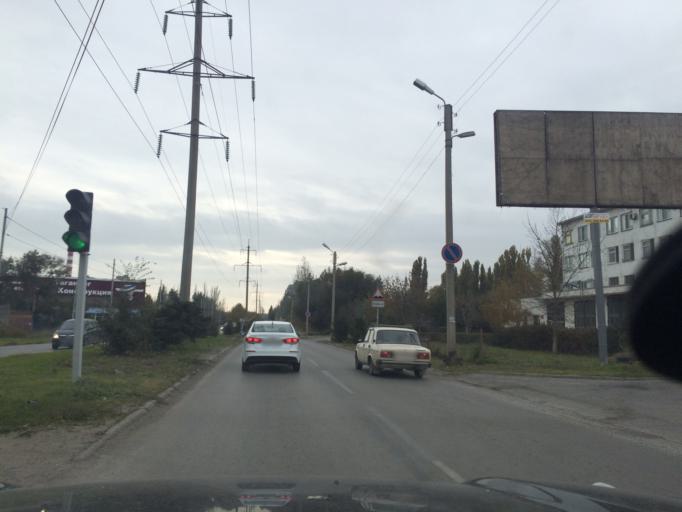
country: RU
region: Rostov
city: Taganrog
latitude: 47.2569
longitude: 38.9246
